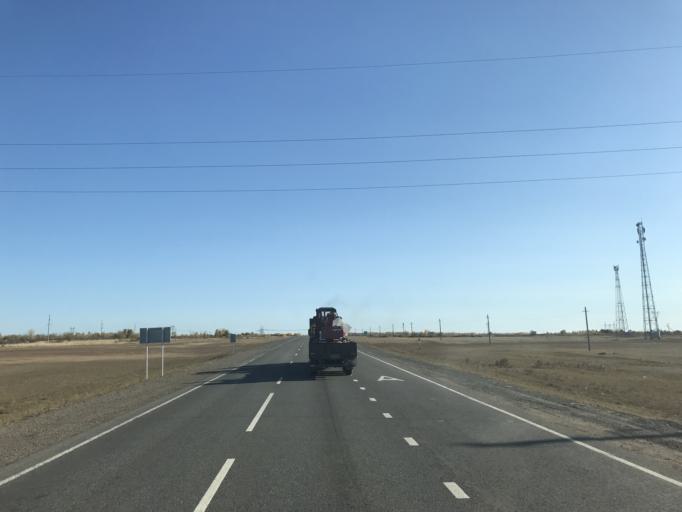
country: KZ
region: Pavlodar
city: Koktobe
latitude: 51.9237
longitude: 77.3374
